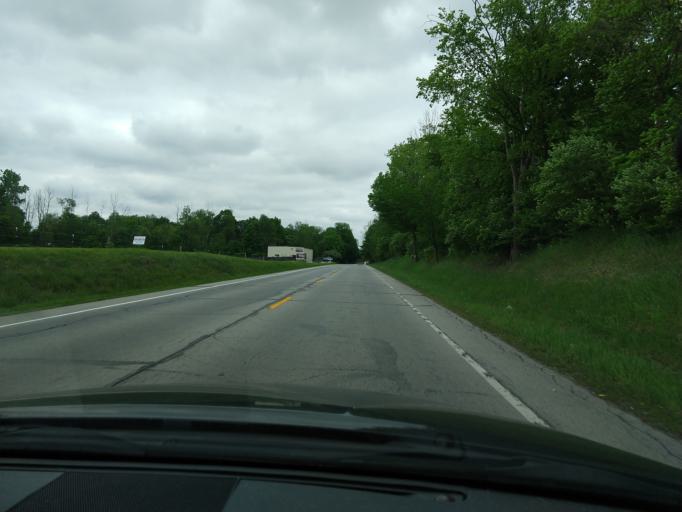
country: US
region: Indiana
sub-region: Hamilton County
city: Noblesville
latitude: 40.0485
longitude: -85.9471
